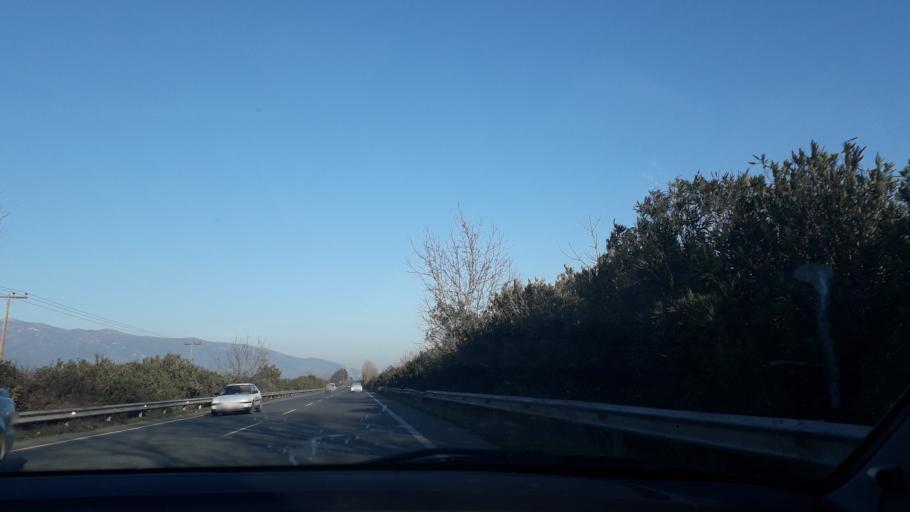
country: GR
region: Central Macedonia
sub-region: Nomos Pellis
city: Mavrovouni
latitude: 40.7917
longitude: 22.1711
